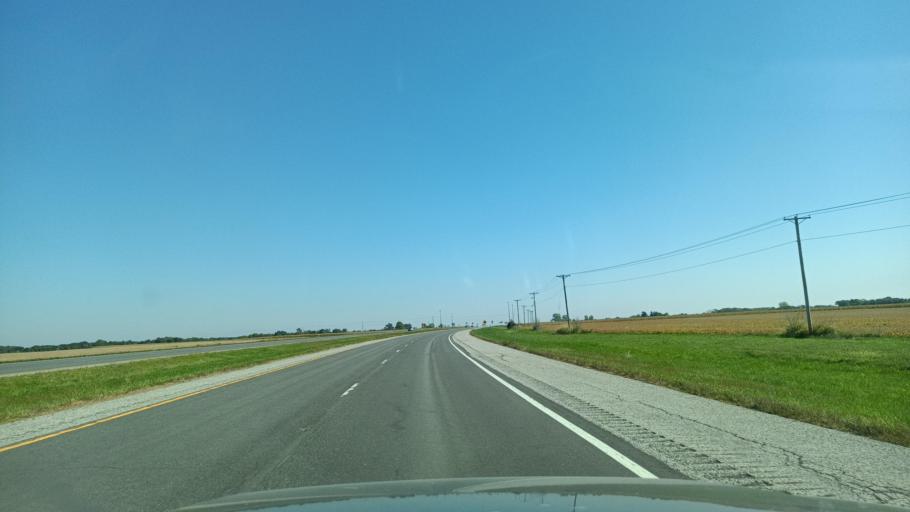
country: US
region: Illinois
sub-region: Adams County
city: Camp Point
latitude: 40.1819
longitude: -91.1882
